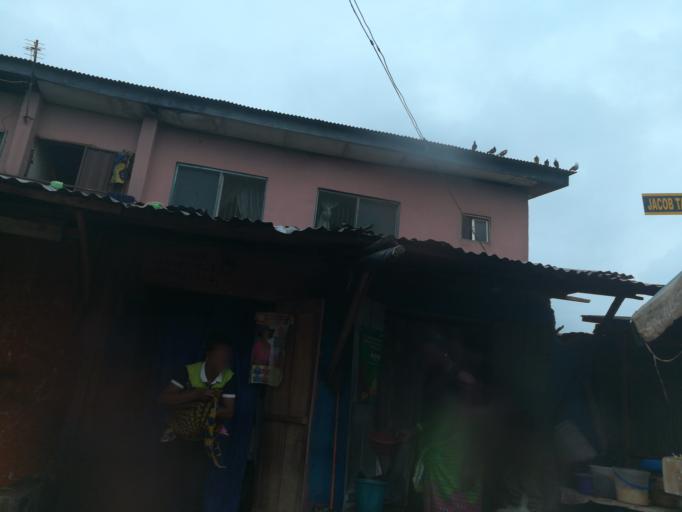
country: NG
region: Lagos
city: Oshodi
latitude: 6.5724
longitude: 3.3424
